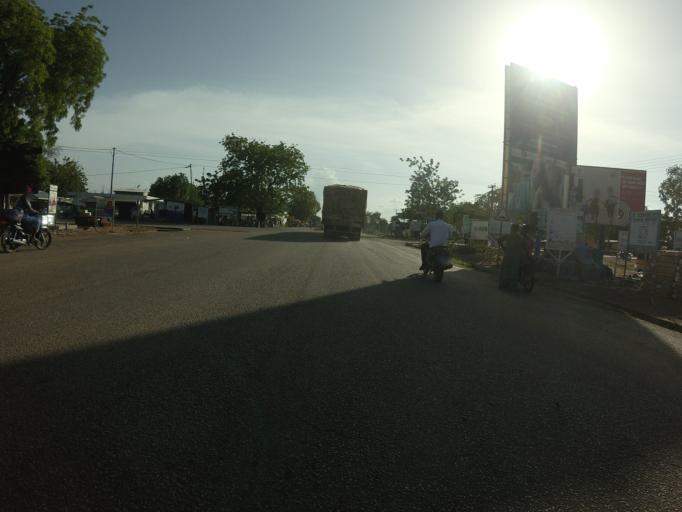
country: GH
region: Upper East
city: Navrongo
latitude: 10.8965
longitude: -1.0896
